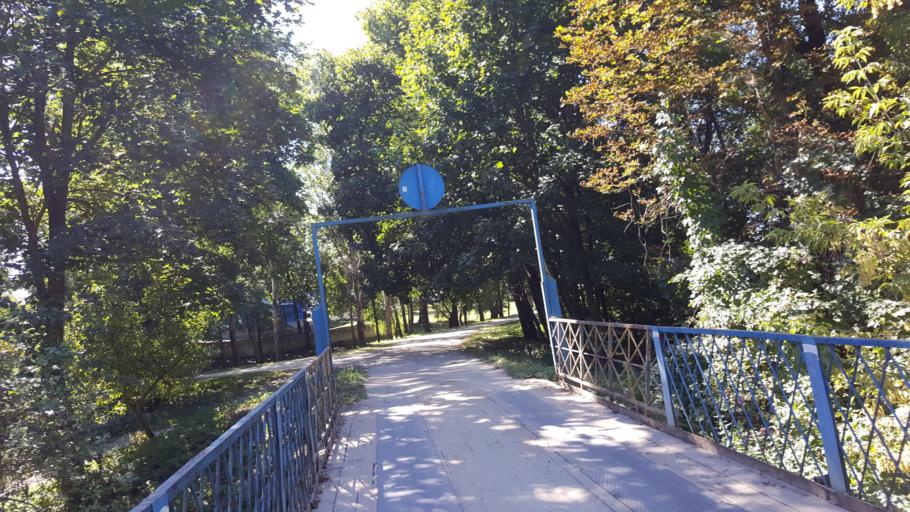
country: PL
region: Lublin Voivodeship
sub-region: Powiat bialski
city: Rokitno
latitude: 52.2243
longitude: 23.3441
